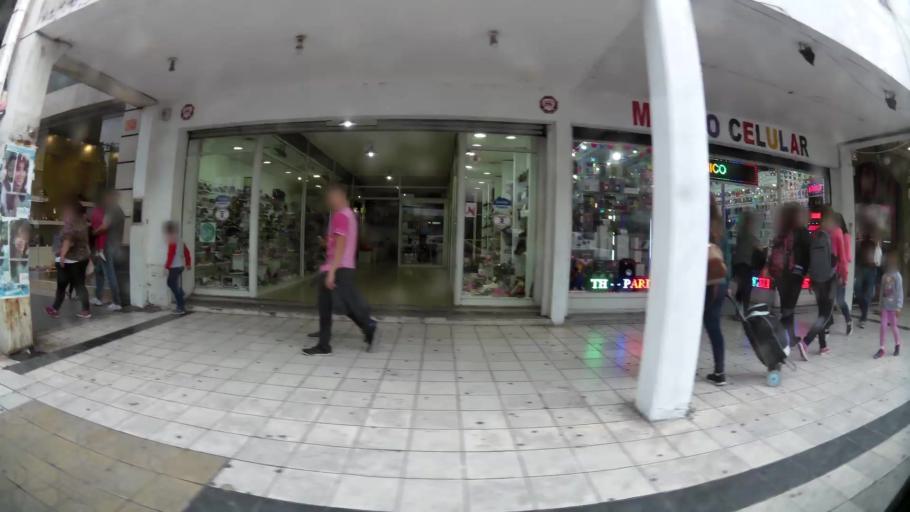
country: AR
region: Buenos Aires
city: San Nicolas de los Arroyos
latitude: -33.3326
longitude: -60.2189
